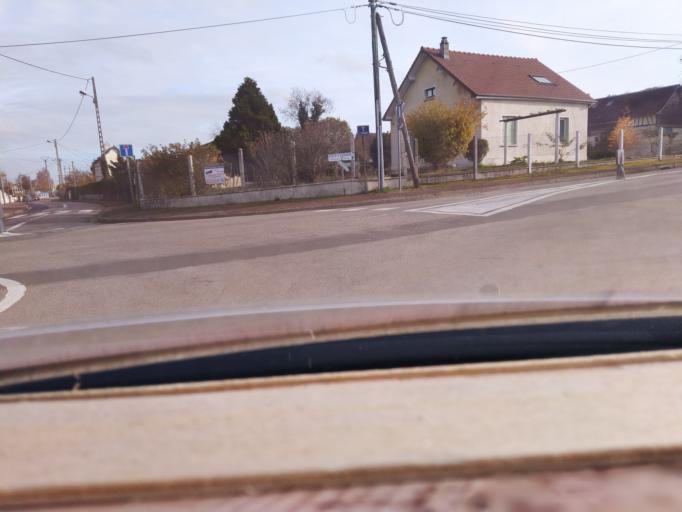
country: FR
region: Haute-Normandie
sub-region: Departement de la Seine-Maritime
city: Yainville
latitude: 49.4584
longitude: 0.8336
